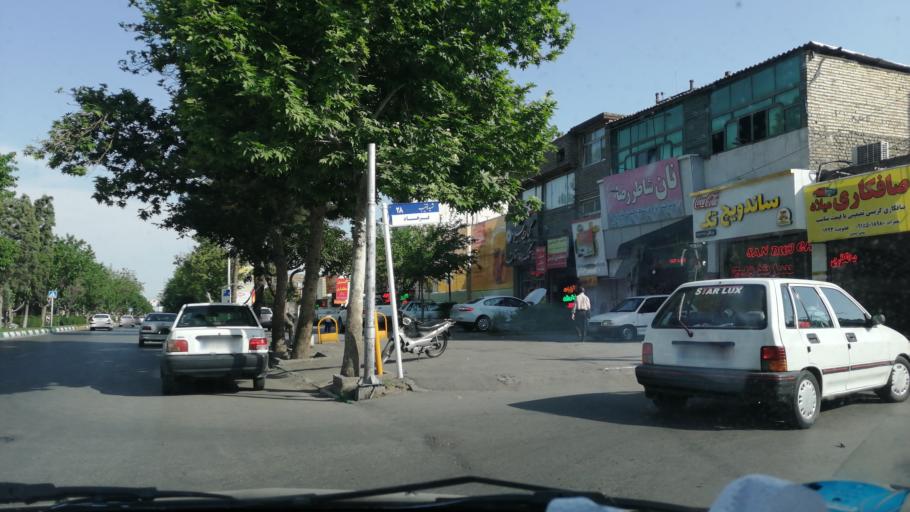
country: IR
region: Razavi Khorasan
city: Mashhad
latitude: 36.3131
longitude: 59.5626
